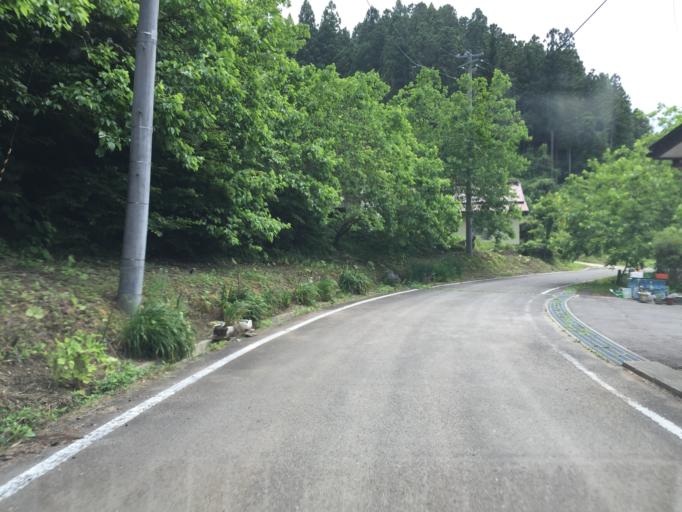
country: JP
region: Miyagi
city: Marumori
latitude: 37.8272
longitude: 140.7314
